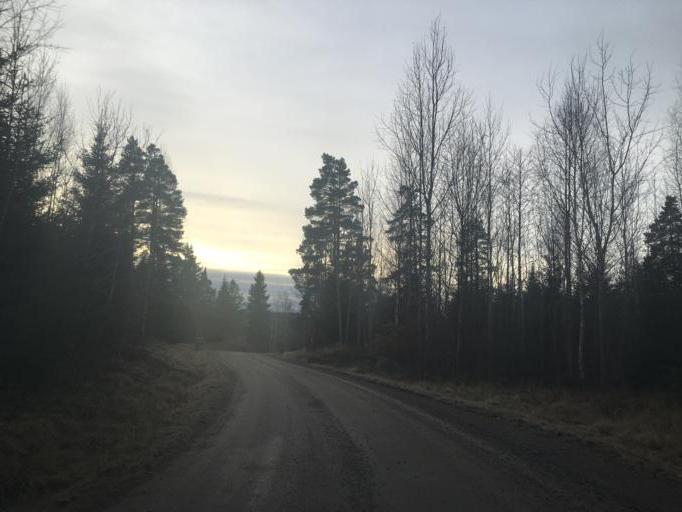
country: SE
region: OEstergoetland
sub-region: Norrkopings Kommun
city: Kimstad
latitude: 58.4194
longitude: 16.0442
